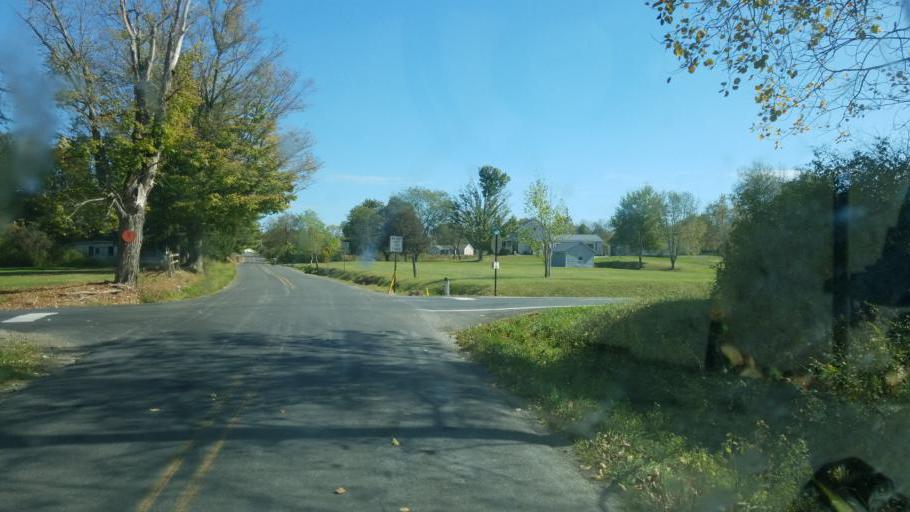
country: US
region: Pennsylvania
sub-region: Mercer County
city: Reynolds Heights
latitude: 41.3695
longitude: -80.3953
